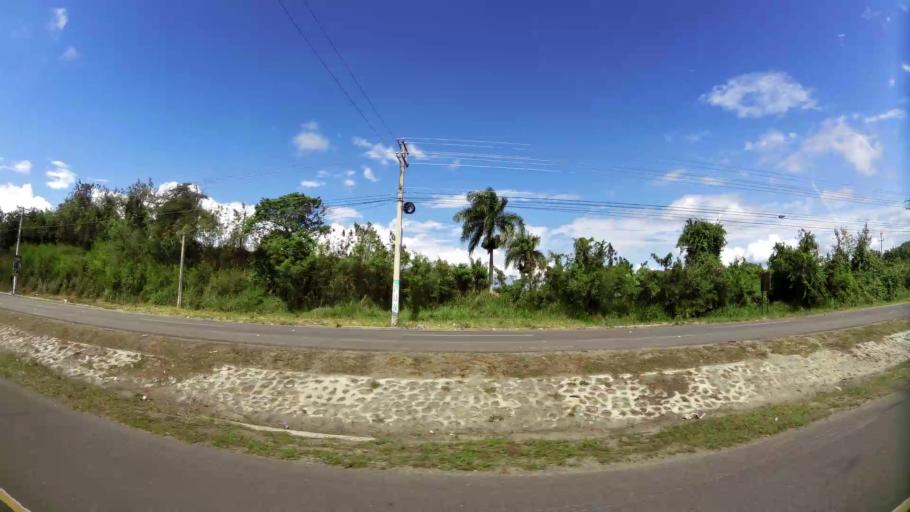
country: DO
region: Santiago
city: Licey al Medio
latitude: 19.3798
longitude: -70.6102
